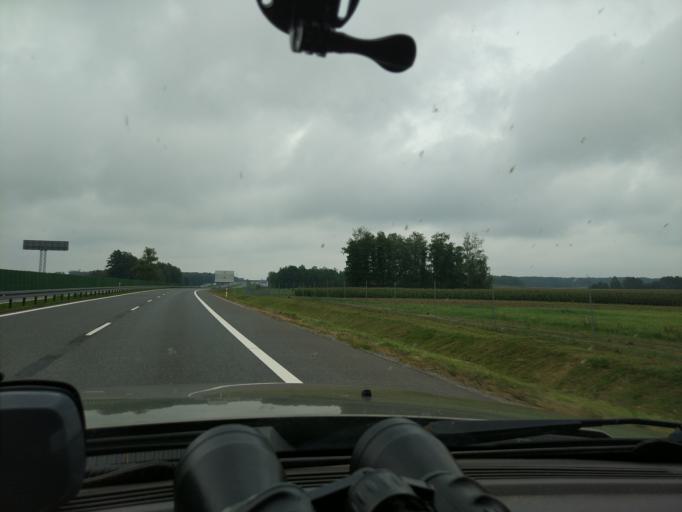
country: PL
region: Podlasie
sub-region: Powiat zambrowski
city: Zambrow
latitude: 53.0181
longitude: 22.3123
